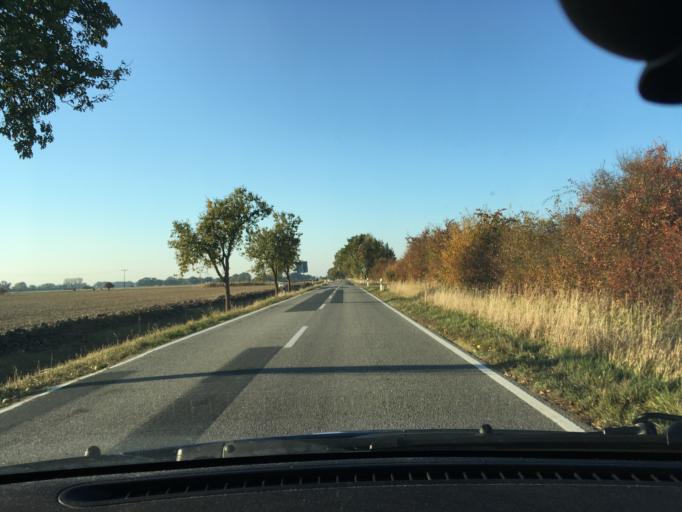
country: DE
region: Lower Saxony
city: Bleckede
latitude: 53.2909
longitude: 10.8063
